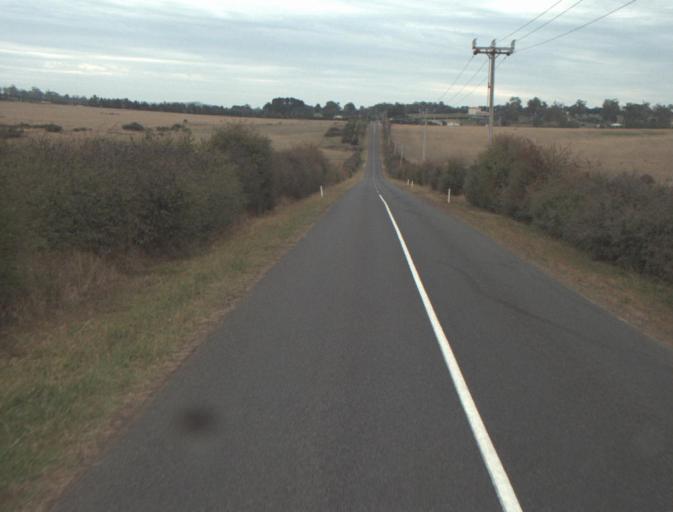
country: AU
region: Tasmania
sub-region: Northern Midlands
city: Evandale
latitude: -41.5153
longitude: 147.2151
